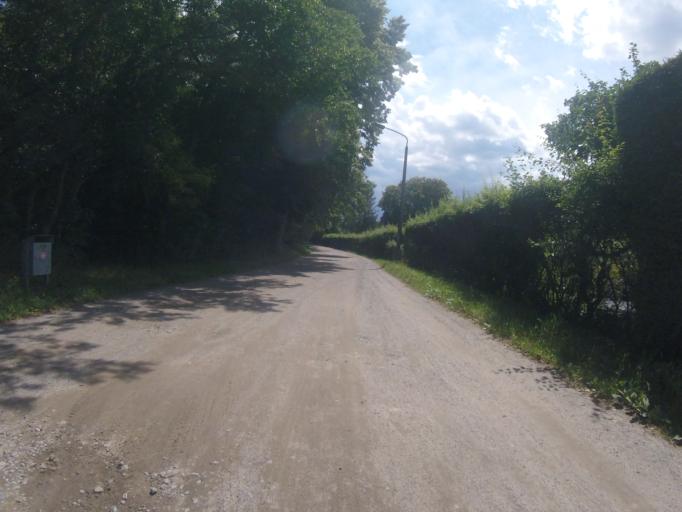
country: DE
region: Brandenburg
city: Bestensee
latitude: 52.2652
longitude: 13.6437
